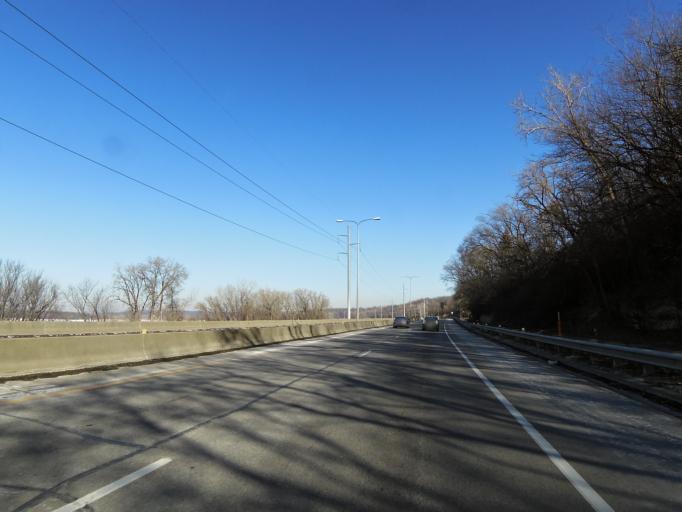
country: US
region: Minnesota
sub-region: Dakota County
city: South Saint Paul
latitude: 44.9130
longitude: -93.0144
